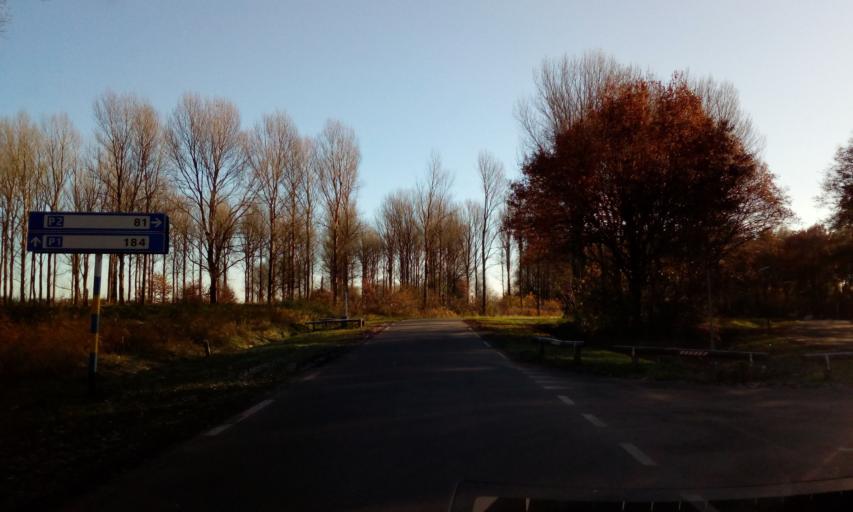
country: NL
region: South Holland
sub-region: Gemeente Zoetermeer
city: Zoetermeer
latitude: 52.0893
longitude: 4.5083
